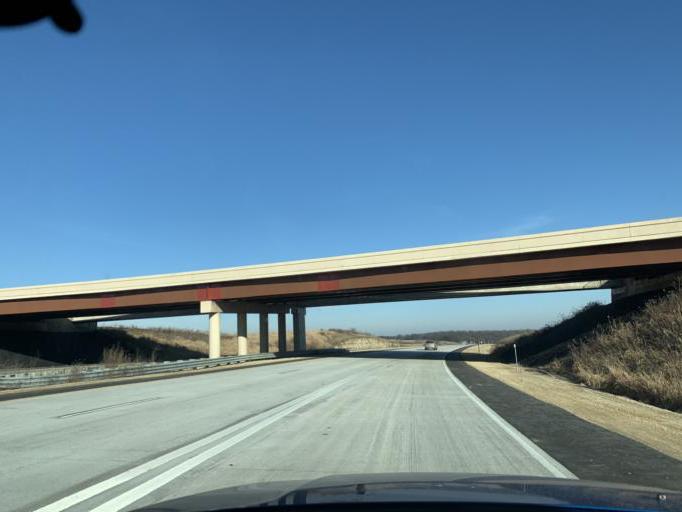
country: US
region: Wisconsin
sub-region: Iowa County
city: Dodgeville
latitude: 42.9363
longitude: -90.1316
